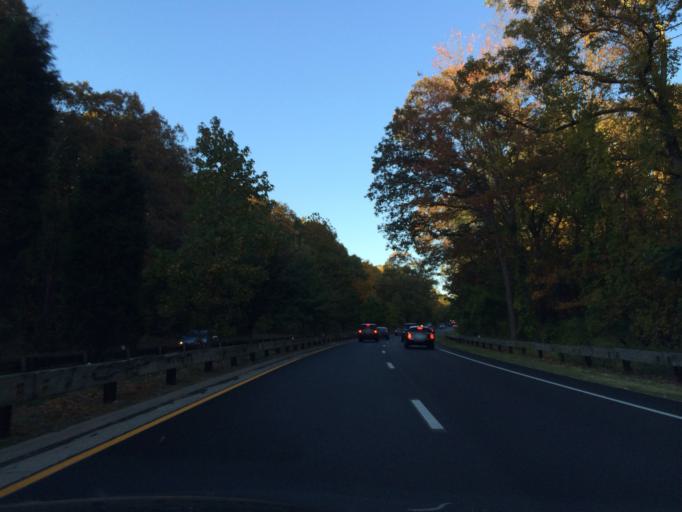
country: US
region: Connecticut
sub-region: Fairfield County
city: Glenville
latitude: 41.0760
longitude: -73.6693
